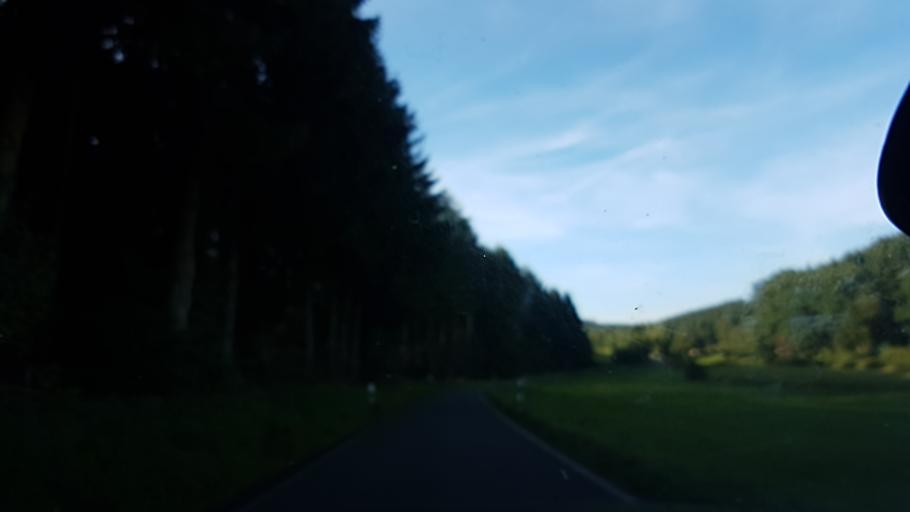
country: DE
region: North Rhine-Westphalia
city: Kierspe
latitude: 51.1386
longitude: 7.5719
